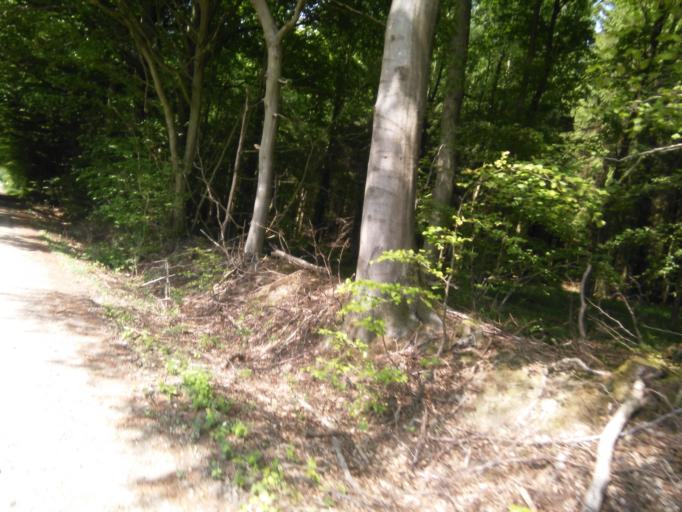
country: DK
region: Central Jutland
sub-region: Favrskov Kommune
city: Hammel
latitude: 56.2688
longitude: 9.9545
